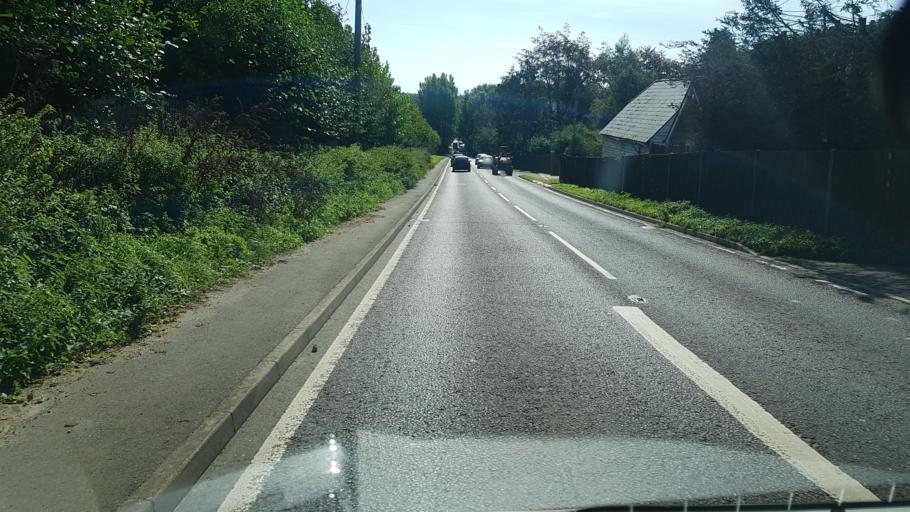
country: GB
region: England
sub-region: Kent
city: Kings Hill
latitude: 51.2614
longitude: 0.3648
